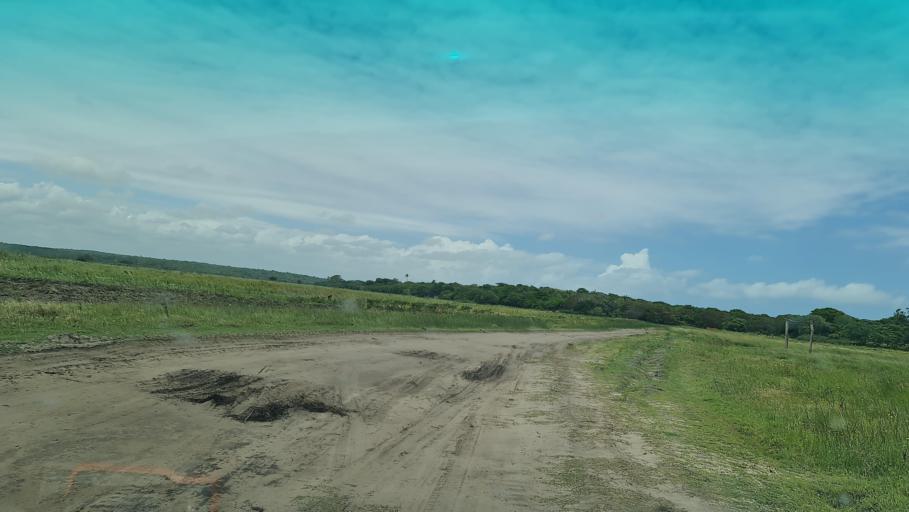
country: MZ
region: Maputo
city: Manhica
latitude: -25.5246
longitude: 32.8571
